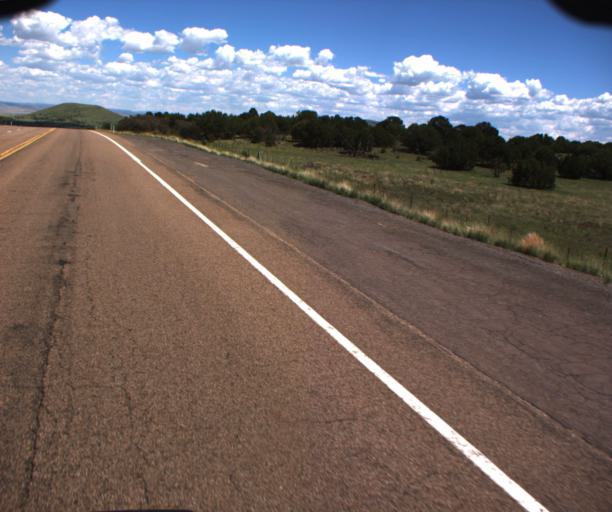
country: US
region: Arizona
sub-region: Apache County
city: Springerville
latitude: 34.2656
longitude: -109.5788
